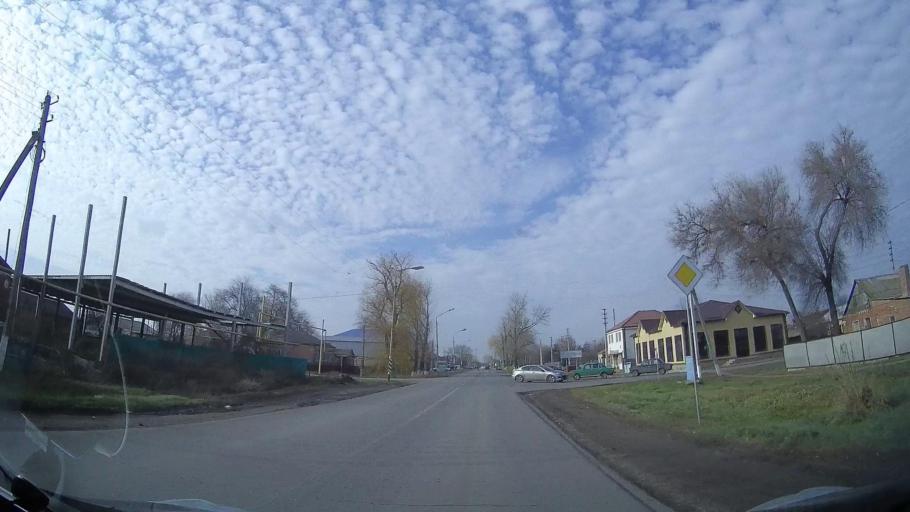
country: RU
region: Rostov
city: Veselyy
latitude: 47.0904
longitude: 40.7463
